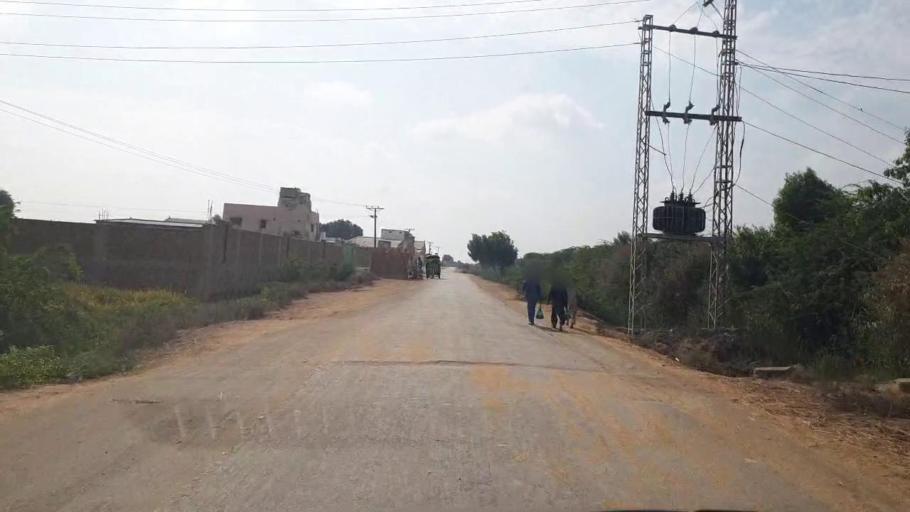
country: PK
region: Sindh
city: Kario
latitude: 24.6501
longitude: 68.5424
